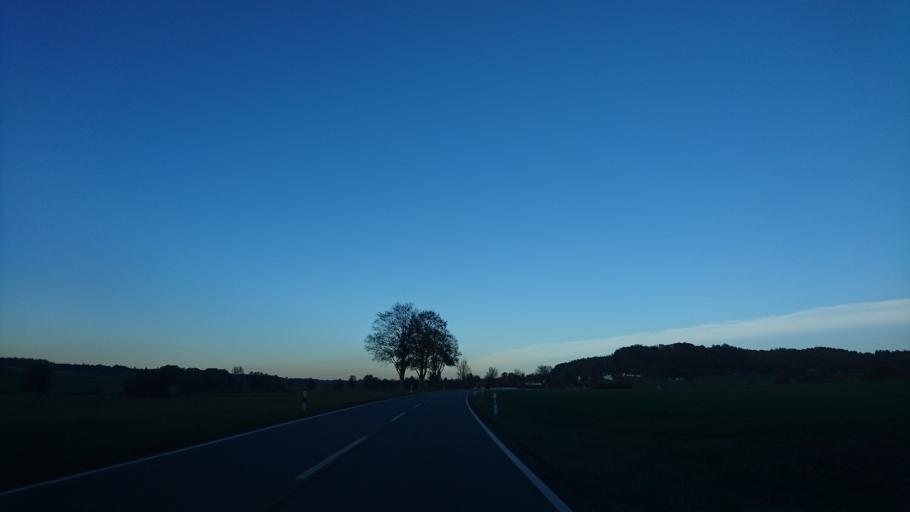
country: DE
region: Bavaria
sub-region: Swabia
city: Dinkelscherben
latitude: 48.3619
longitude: 10.5736
